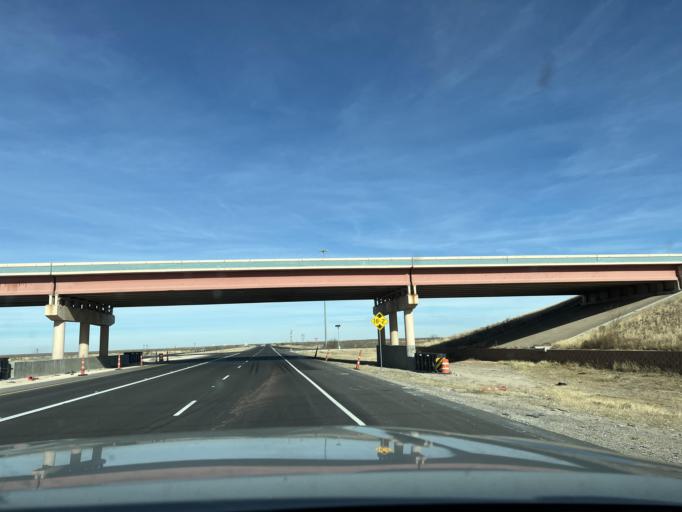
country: US
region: Texas
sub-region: Ector County
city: Gardendale
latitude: 32.0234
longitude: -102.4302
